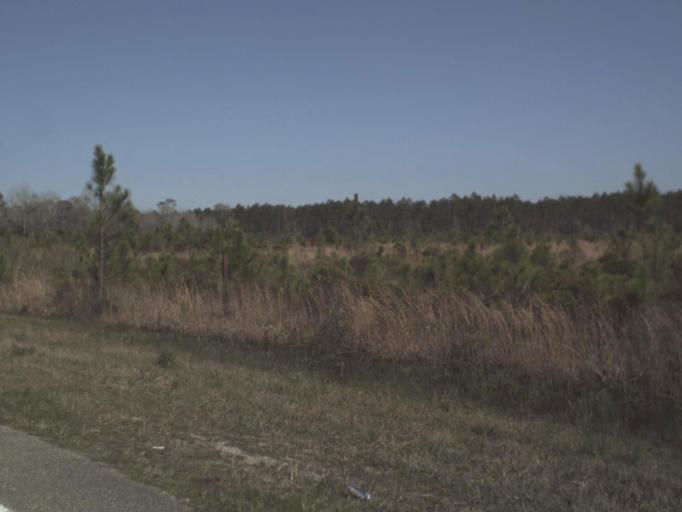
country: US
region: Florida
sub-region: Gulf County
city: Port Saint Joe
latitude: 29.8701
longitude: -85.2332
